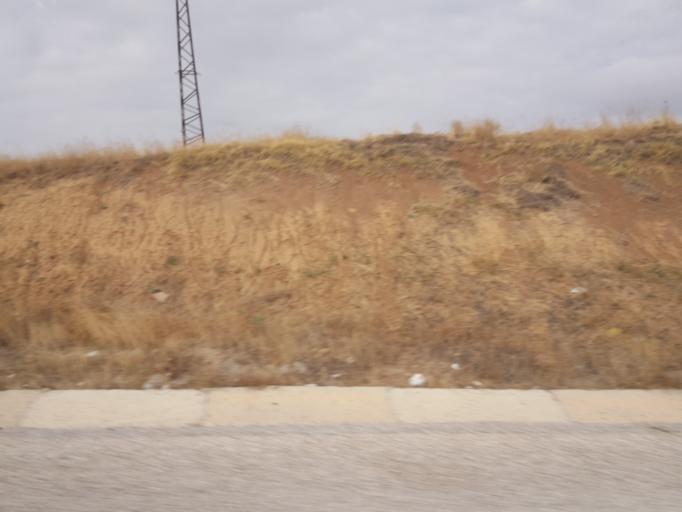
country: TR
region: Kirikkale
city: Bahsili
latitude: 39.7086
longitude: 33.4269
